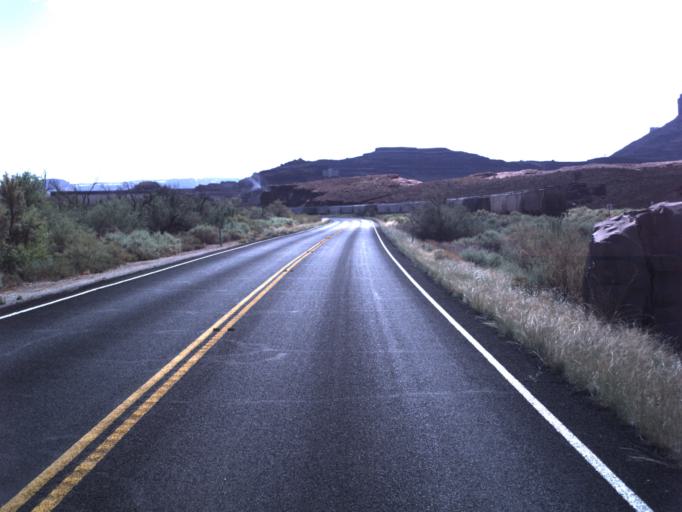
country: US
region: Utah
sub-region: Grand County
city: Moab
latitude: 38.5352
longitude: -109.6558
